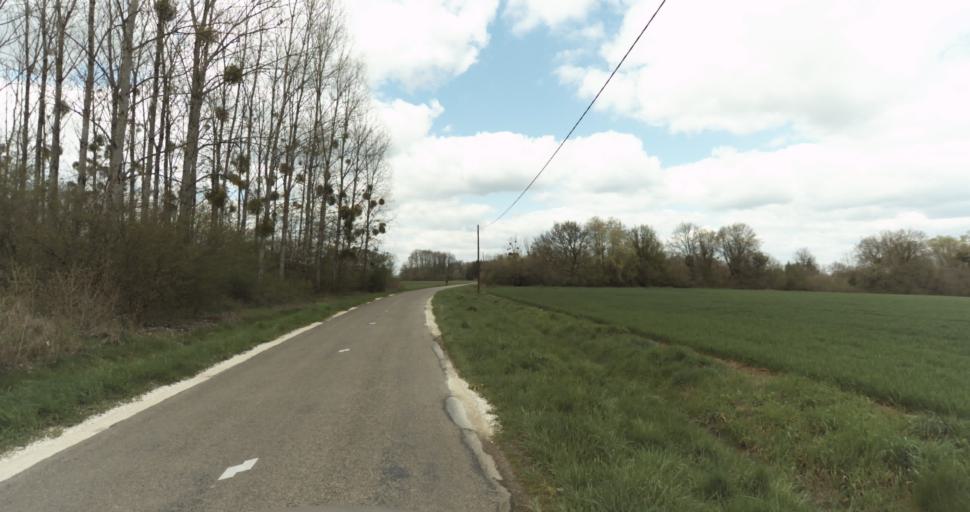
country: FR
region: Bourgogne
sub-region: Departement de la Cote-d'Or
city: Auxonne
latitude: 47.1783
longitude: 5.4208
